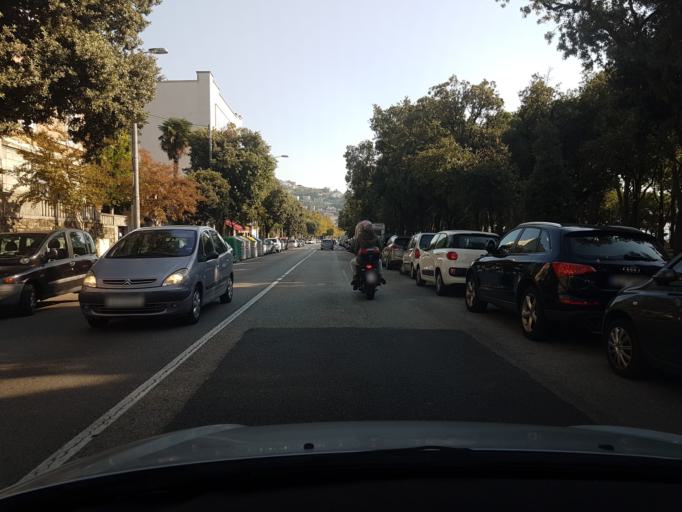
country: IT
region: Friuli Venezia Giulia
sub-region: Provincia di Trieste
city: Prosecco-Contovello
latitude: 45.6841
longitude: 13.7501
